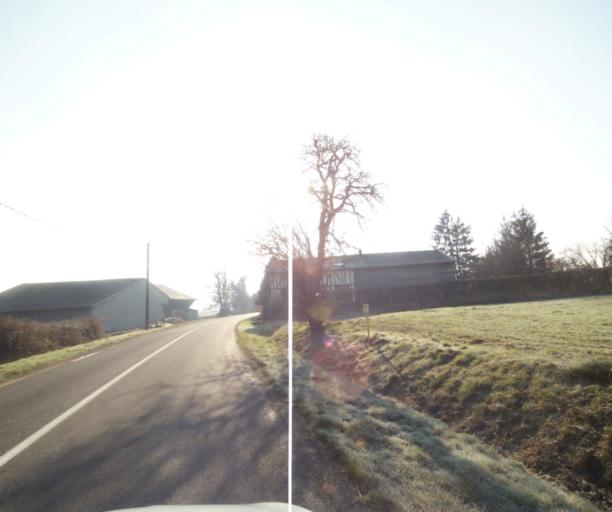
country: FR
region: Champagne-Ardenne
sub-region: Departement de la Haute-Marne
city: Montier-en-Der
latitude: 48.4645
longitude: 4.7647
